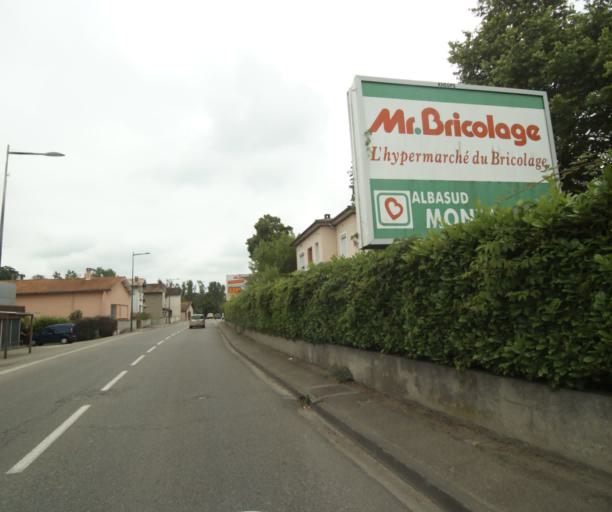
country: FR
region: Midi-Pyrenees
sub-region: Departement du Tarn-et-Garonne
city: Montauban
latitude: 44.0107
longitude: 1.3549
